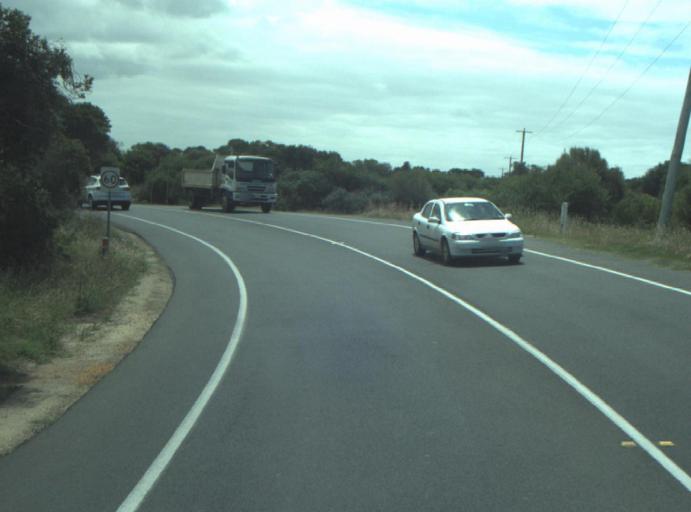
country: AU
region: Victoria
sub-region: Greater Geelong
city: Leopold
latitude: -38.2796
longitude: 144.5008
